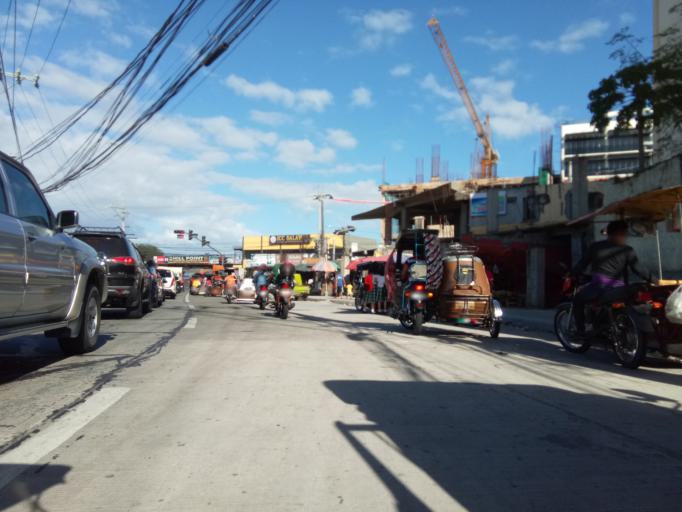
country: PH
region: Calabarzon
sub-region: Province of Cavite
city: Dasmarinas
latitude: 14.3534
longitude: 120.9807
